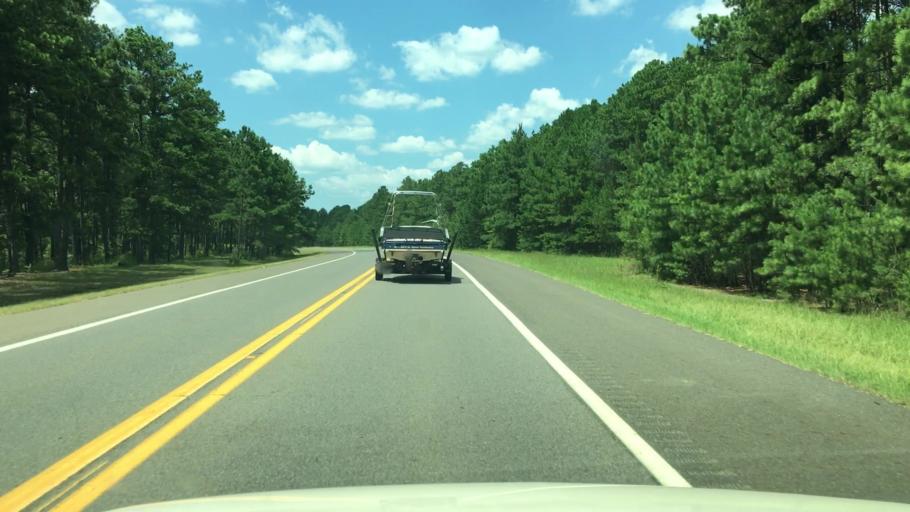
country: US
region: Arkansas
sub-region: Clark County
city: Arkadelphia
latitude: 34.2236
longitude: -93.0875
